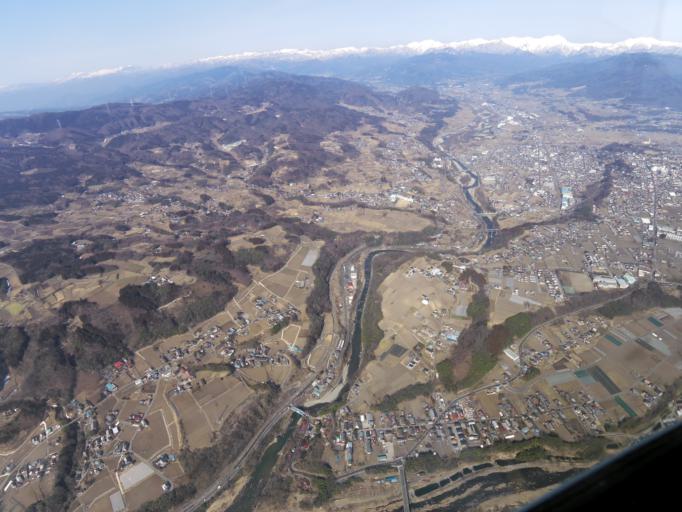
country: JP
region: Gunma
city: Numata
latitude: 36.6169
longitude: 139.0477
